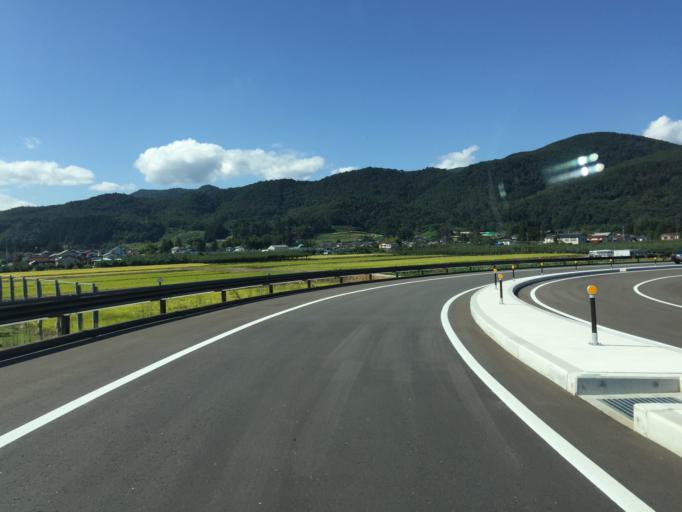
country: JP
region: Fukushima
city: Fukushima-shi
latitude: 37.8001
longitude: 140.4101
